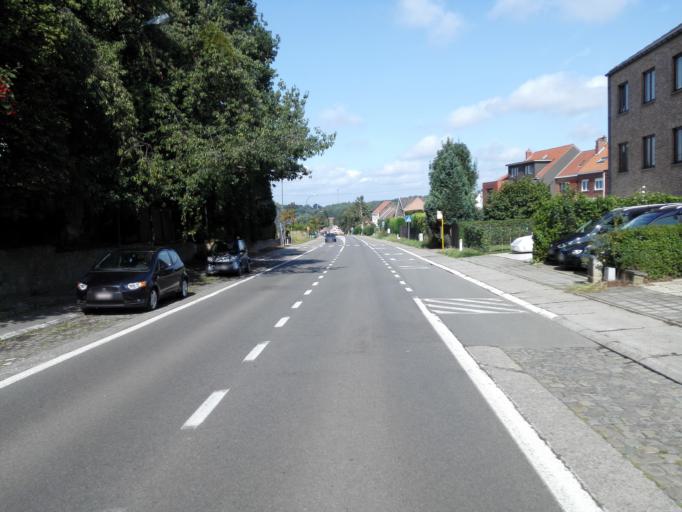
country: BE
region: Flanders
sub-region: Provincie Vlaams-Brabant
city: Wemmel
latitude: 50.9136
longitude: 4.2965
